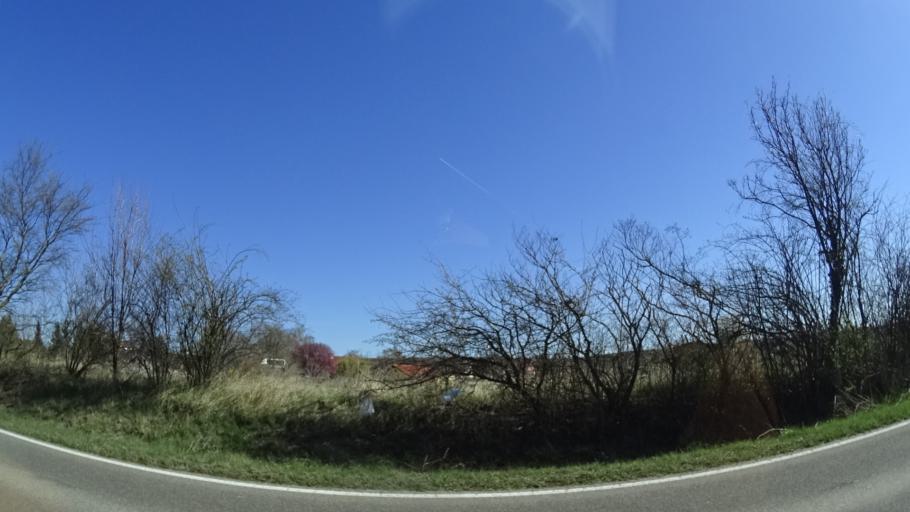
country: DE
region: Rheinland-Pfalz
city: Hillesheim
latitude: 49.7718
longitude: 8.2547
